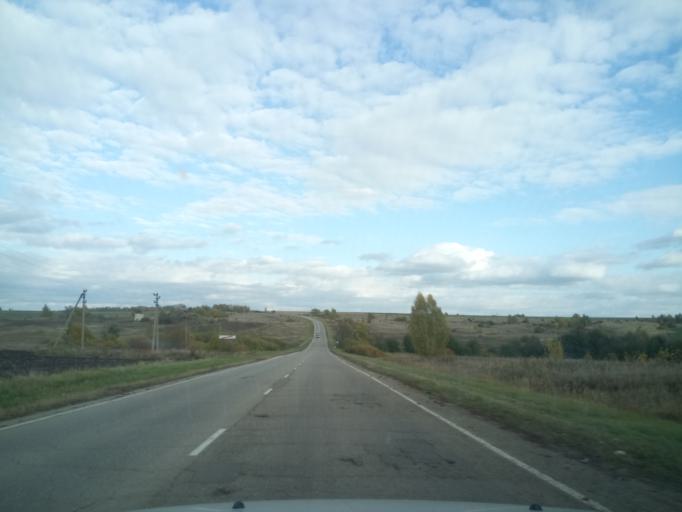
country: RU
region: Nizjnij Novgorod
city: Bol'shoye Boldino
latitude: 54.9643
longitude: 45.2305
